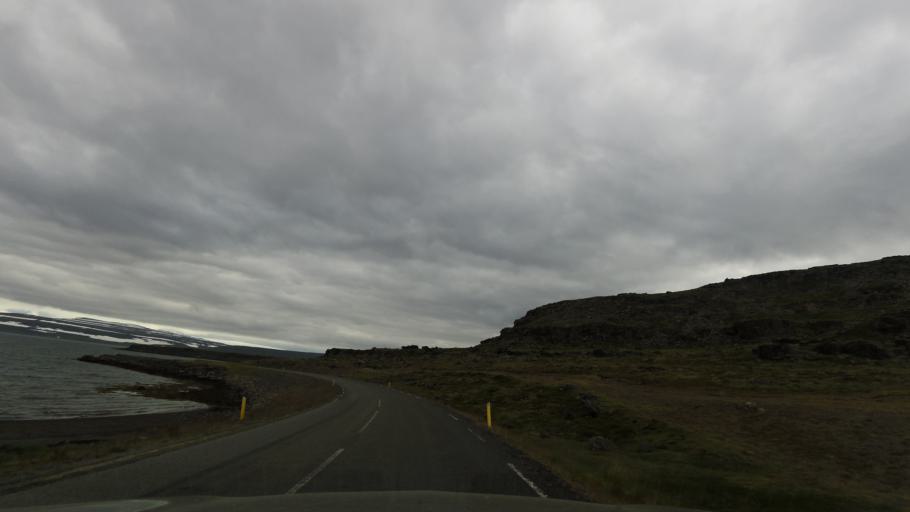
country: IS
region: Westfjords
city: Isafjoerdur
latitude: 65.9726
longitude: -22.5890
